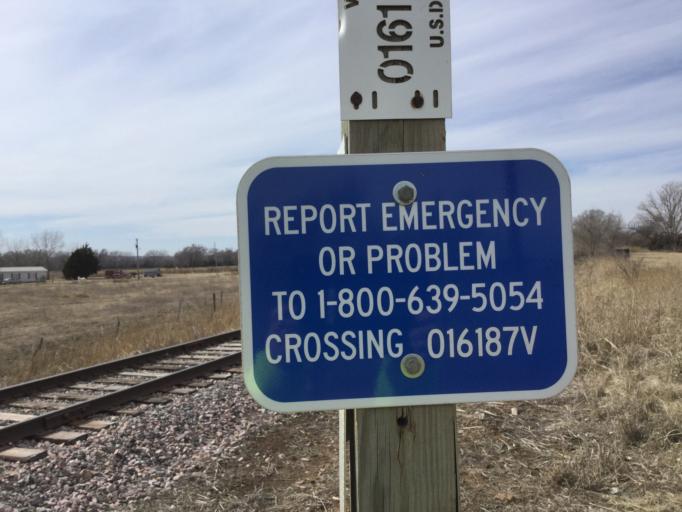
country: US
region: Kansas
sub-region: Barber County
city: Medicine Lodge
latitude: 37.2600
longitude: -98.5688
